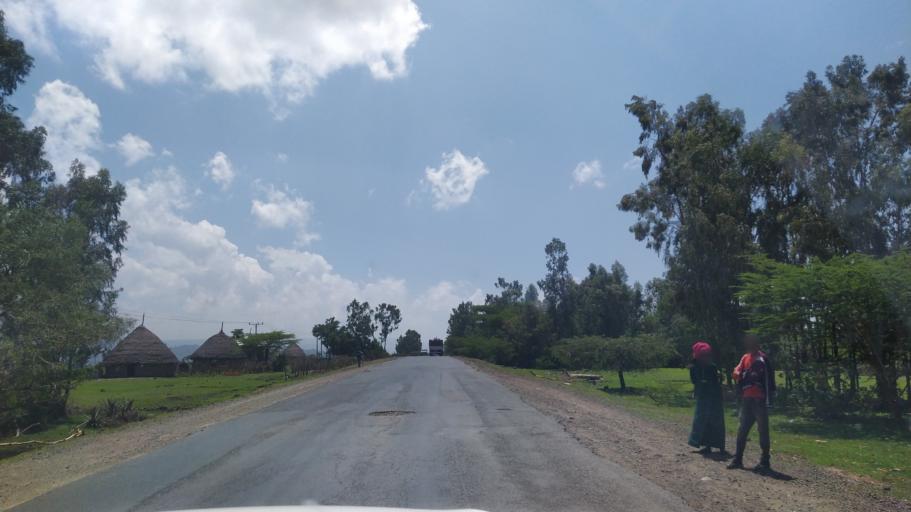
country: ET
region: Southern Nations, Nationalities, and People's Region
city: Butajira
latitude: 7.7623
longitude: 38.1339
